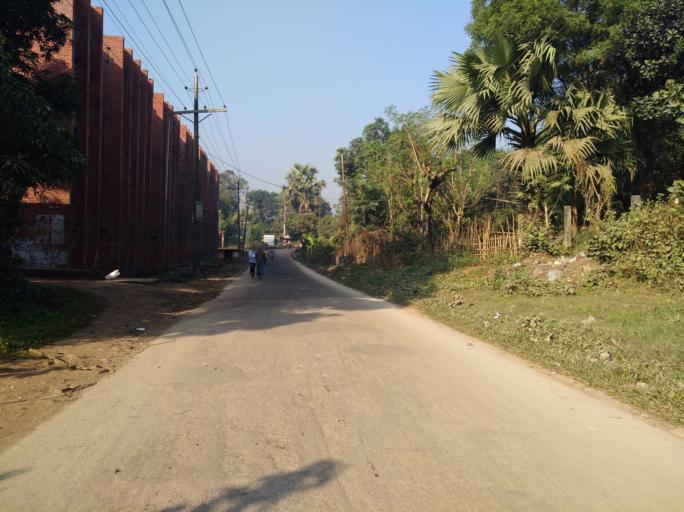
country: BD
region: Dhaka
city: Tungi
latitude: 23.8955
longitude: 90.2688
